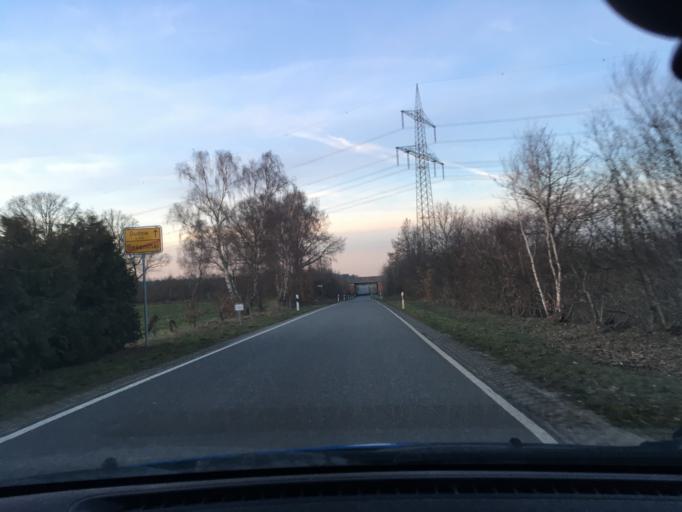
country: DE
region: Schleswig-Holstein
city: Besenthal
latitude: 53.5326
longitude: 10.7420
